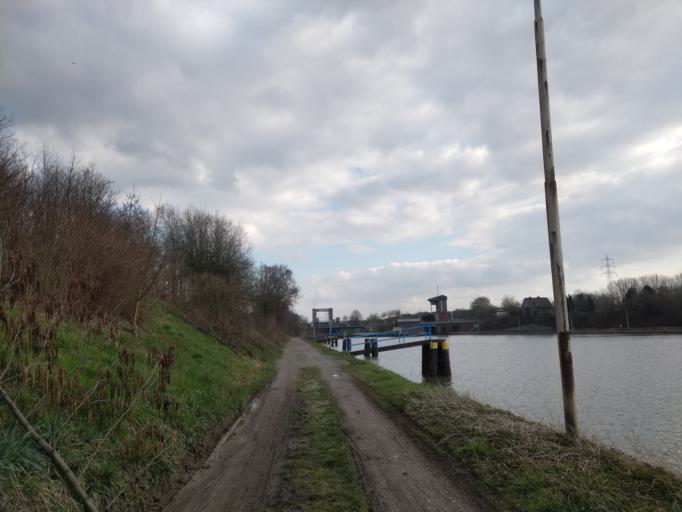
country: DE
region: North Rhine-Westphalia
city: Castrop-Rauxel
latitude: 51.6217
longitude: 7.3289
